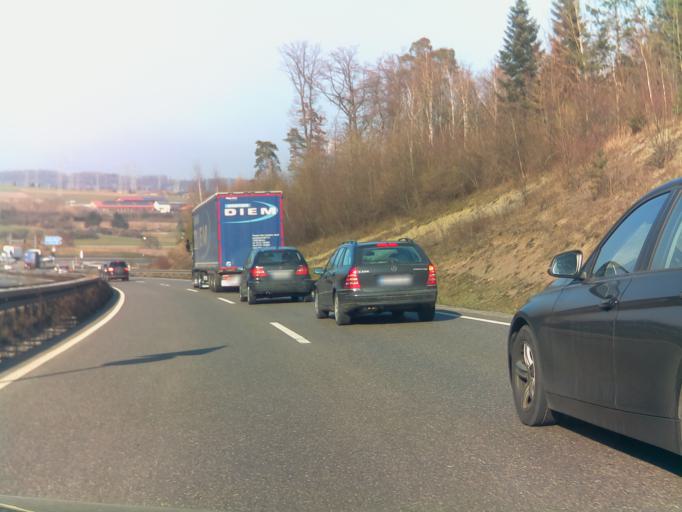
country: DE
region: Baden-Wuerttemberg
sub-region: Regierungsbezirk Stuttgart
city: Leonberg
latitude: 48.7852
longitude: 8.9800
